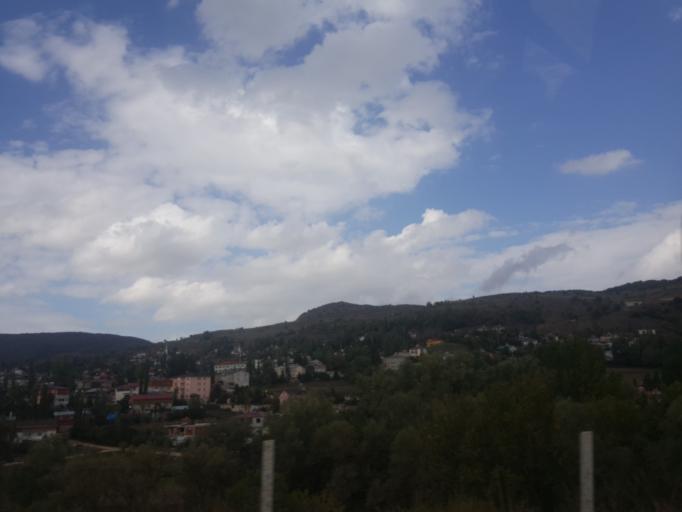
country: TR
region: Tokat
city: Bereketli
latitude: 40.5352
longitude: 37.2969
